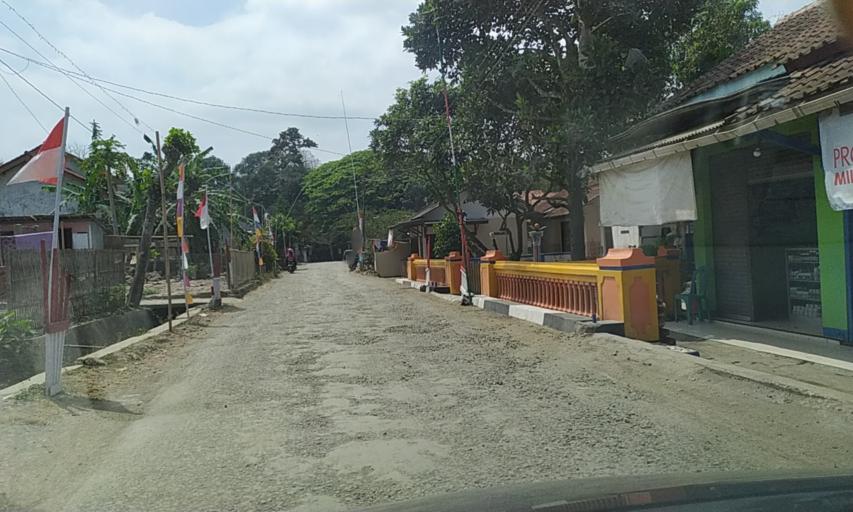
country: ID
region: Central Java
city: Watuagung
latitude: -7.5940
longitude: 109.1150
